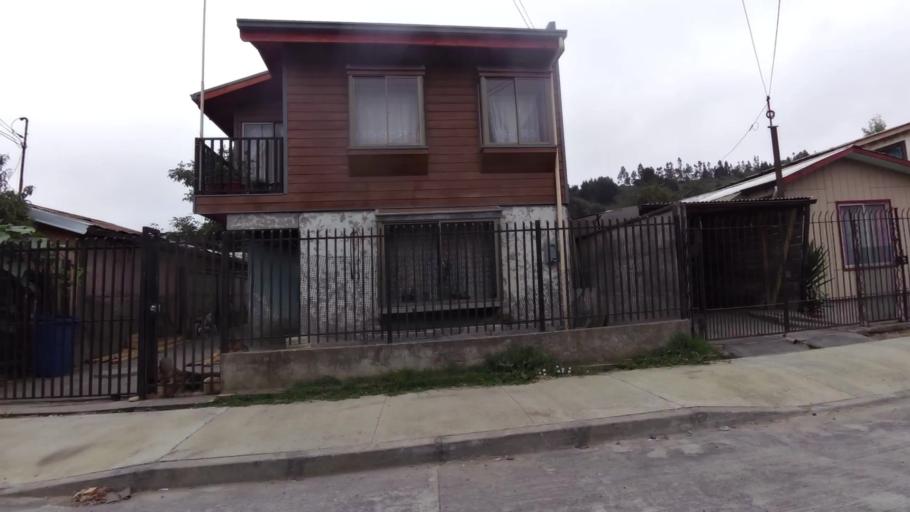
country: CL
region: Biobio
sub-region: Provincia de Concepcion
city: Concepcion
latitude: -36.8329
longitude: -73.0103
